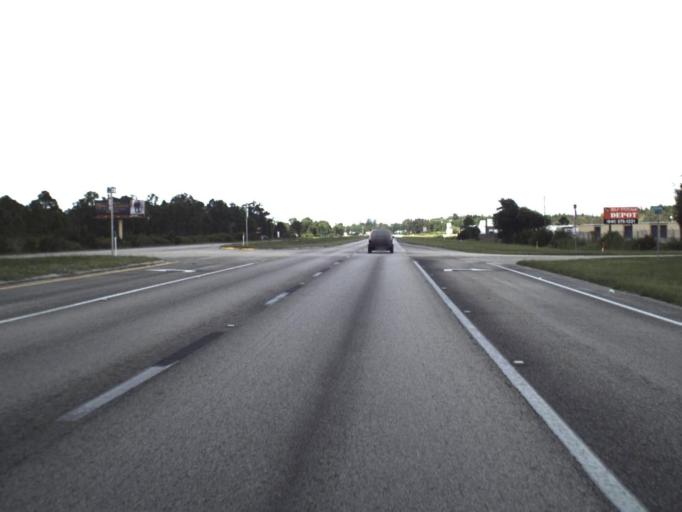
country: US
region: Florida
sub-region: Charlotte County
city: Charlotte Park
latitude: 26.8498
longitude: -81.9823
